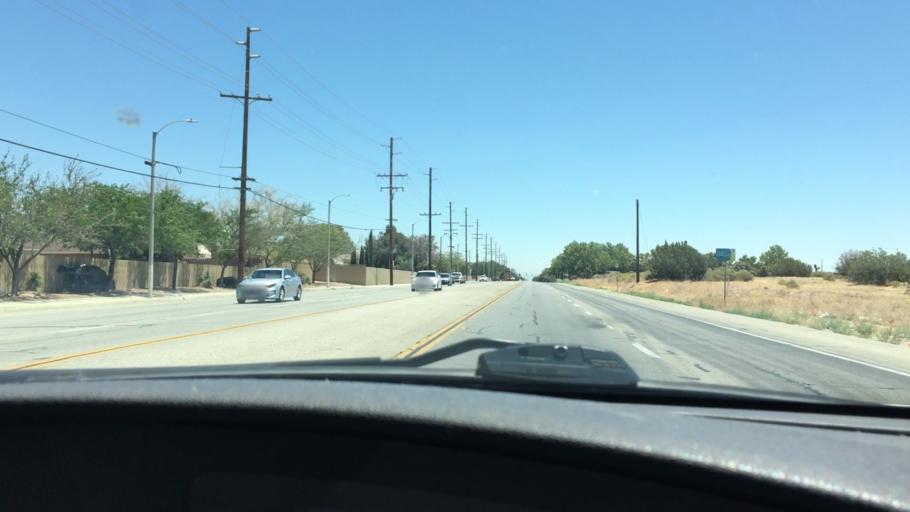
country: US
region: California
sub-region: Los Angeles County
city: Quartz Hill
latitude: 34.6601
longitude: -118.2002
